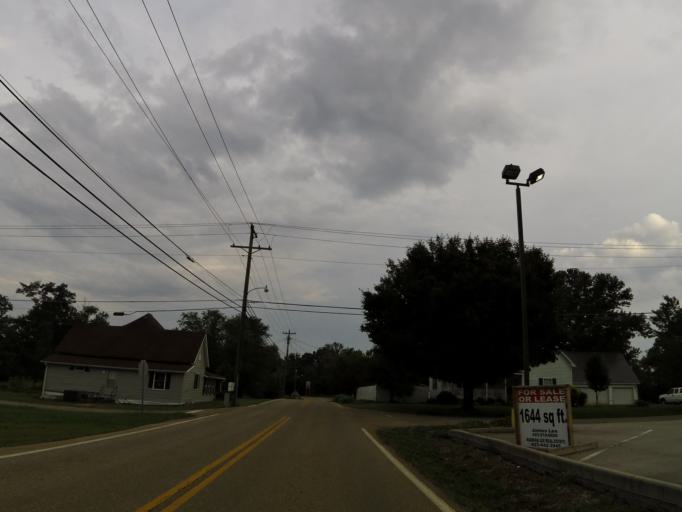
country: US
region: Tennessee
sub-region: Loudon County
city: Greenback
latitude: 35.6610
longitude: -84.1697
